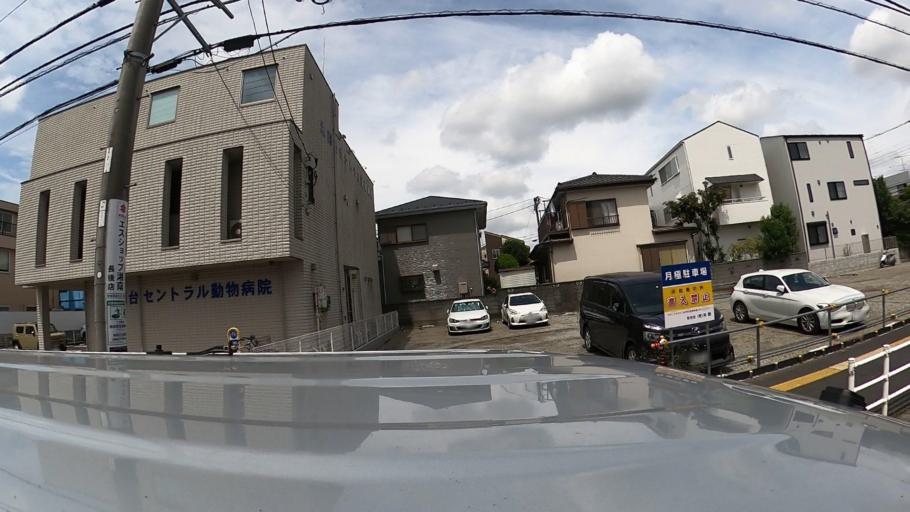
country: JP
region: Kanagawa
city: Fujisawa
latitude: 35.4021
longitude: 139.4697
